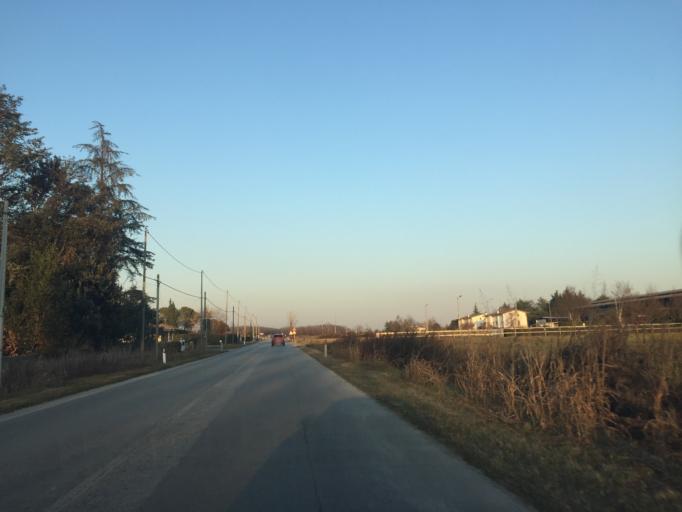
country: IT
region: Friuli Venezia Giulia
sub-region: Provincia di Pordenone
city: Vigonovo-Fontanafredda
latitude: 45.9966
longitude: 12.5555
